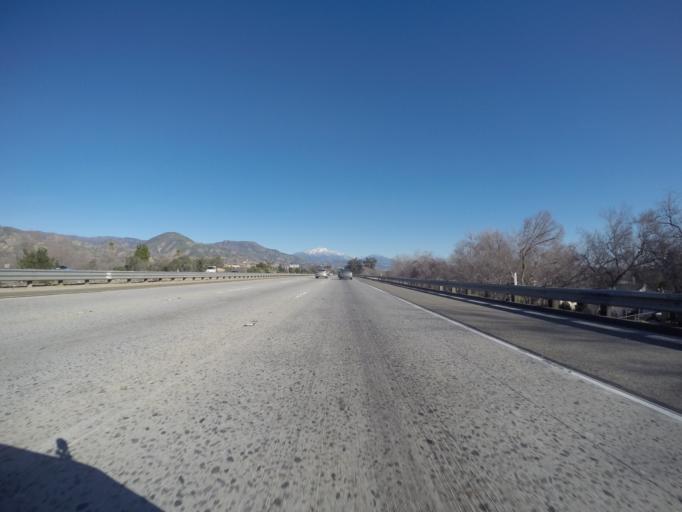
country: US
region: California
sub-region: San Bernardino County
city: San Bernardino
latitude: 34.1443
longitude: -117.2645
